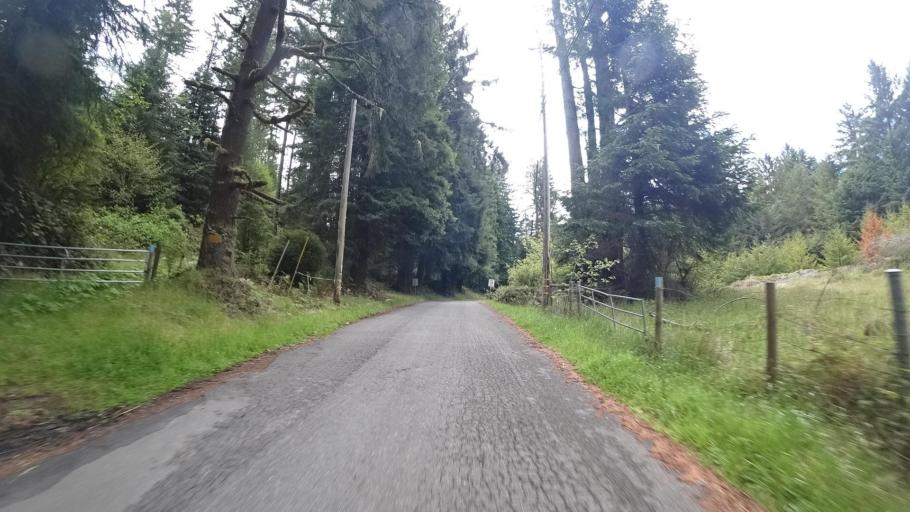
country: US
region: California
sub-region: Humboldt County
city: Bayside
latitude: 40.8489
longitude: -124.0286
